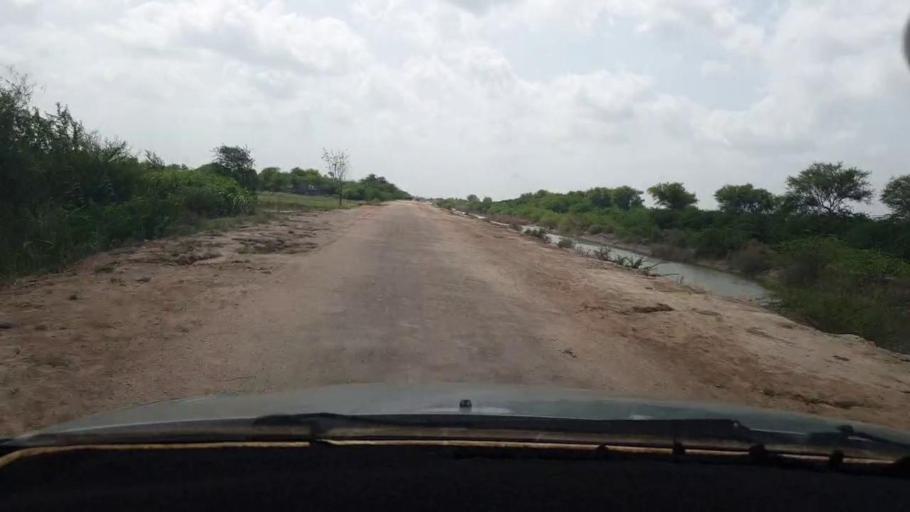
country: PK
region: Sindh
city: Tando Bago
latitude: 24.7264
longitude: 69.1347
